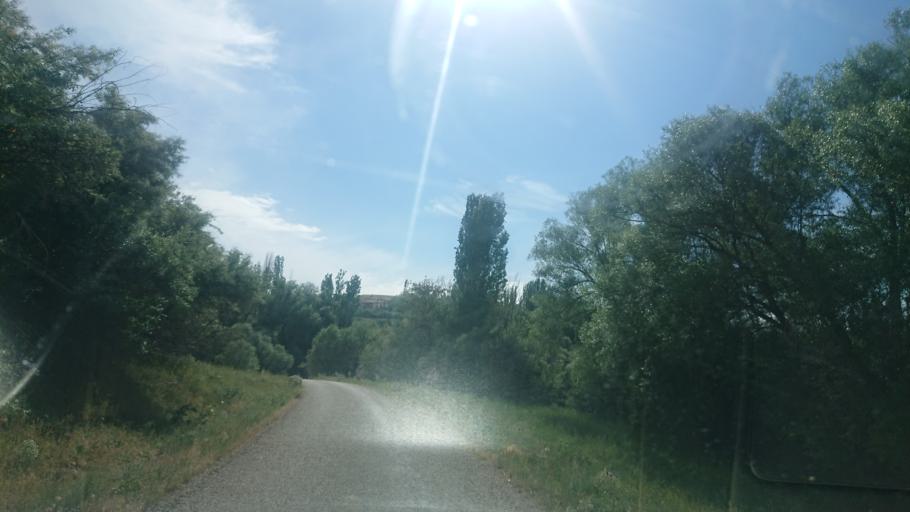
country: TR
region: Aksaray
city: Ortakoy
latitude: 38.8092
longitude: 33.9876
